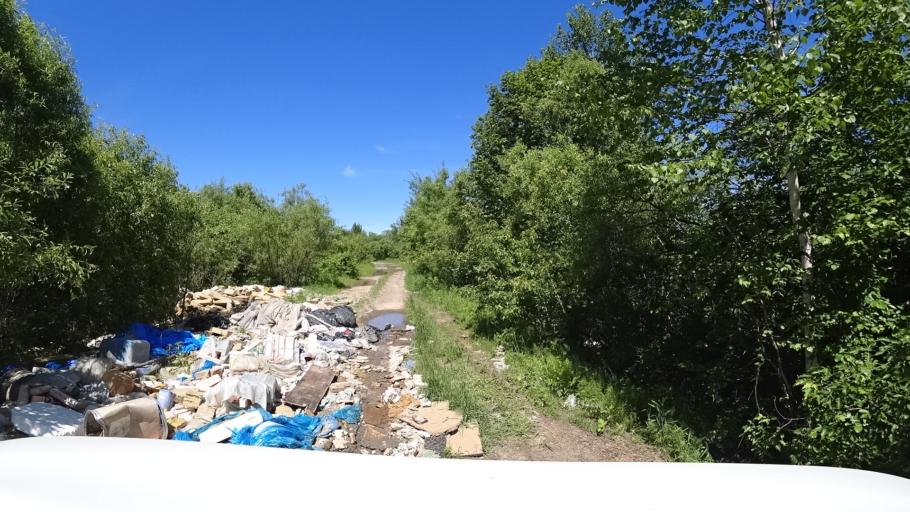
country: RU
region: Khabarovsk Krai
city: Topolevo
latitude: 48.4875
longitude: 135.1771
